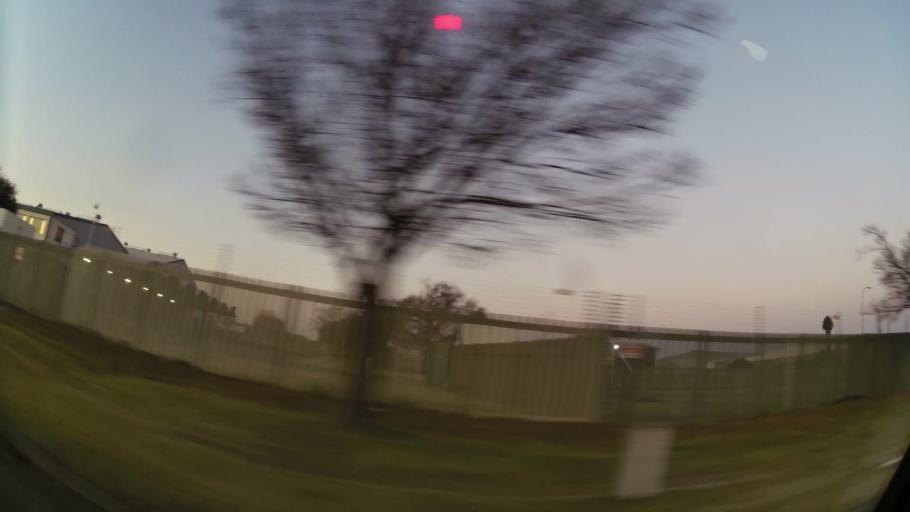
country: ZA
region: Gauteng
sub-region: Ekurhuleni Metropolitan Municipality
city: Germiston
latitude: -26.2726
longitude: 28.1743
